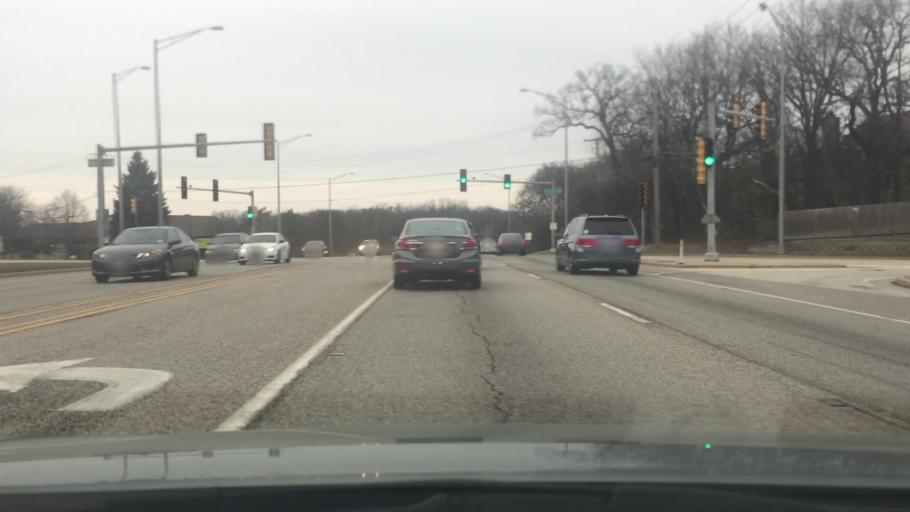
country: US
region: Illinois
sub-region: Kane County
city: Elgin
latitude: 42.0472
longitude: -88.3411
